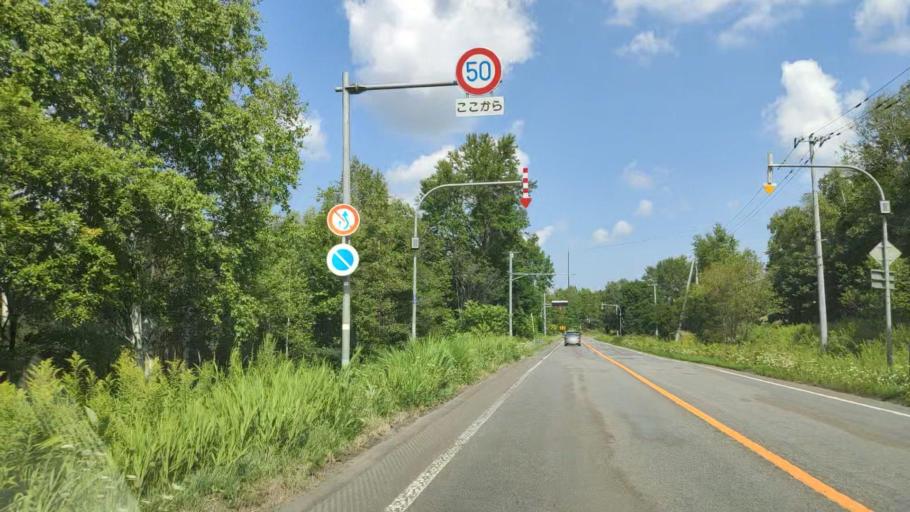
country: JP
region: Hokkaido
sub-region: Asahikawa-shi
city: Asahikawa
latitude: 43.5804
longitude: 142.4378
